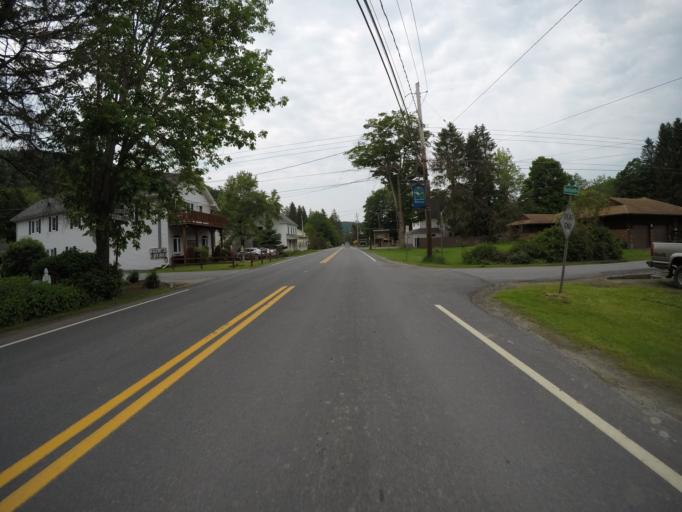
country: US
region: New York
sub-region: Sullivan County
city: Livingston Manor
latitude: 41.9477
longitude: -74.9119
